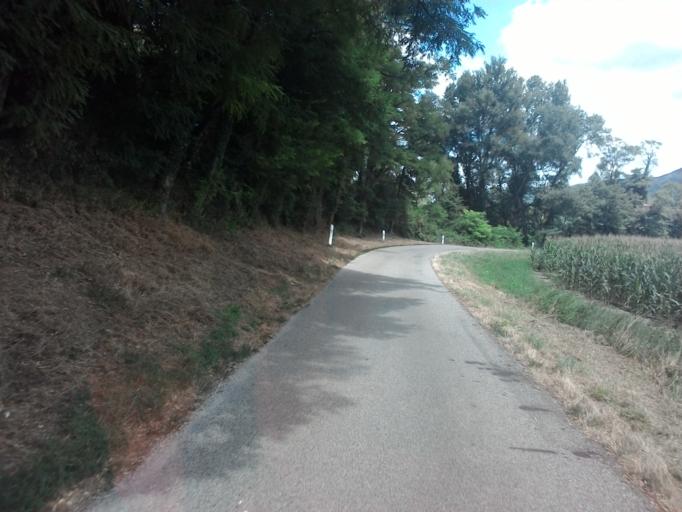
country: FR
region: Rhone-Alpes
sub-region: Departement de l'Ain
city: Lagnieu
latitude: 45.8811
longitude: 5.3478
